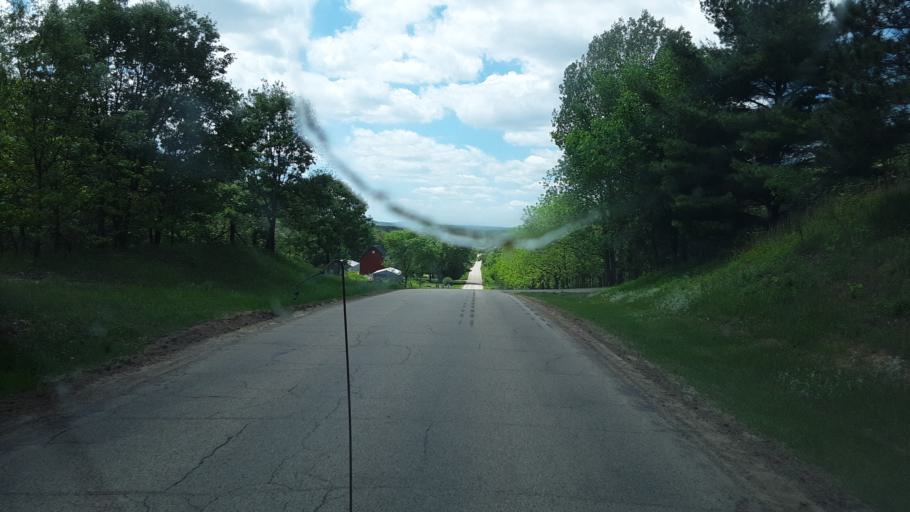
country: US
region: Wisconsin
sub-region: Sauk County
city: Reedsburg
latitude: 43.5767
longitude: -90.0195
